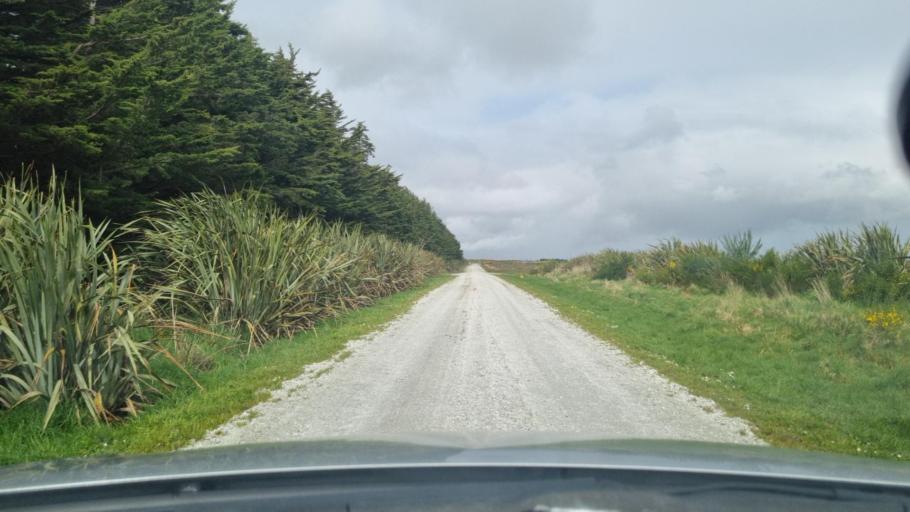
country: NZ
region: Southland
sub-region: Invercargill City
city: Bluff
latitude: -46.5157
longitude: 168.3594
